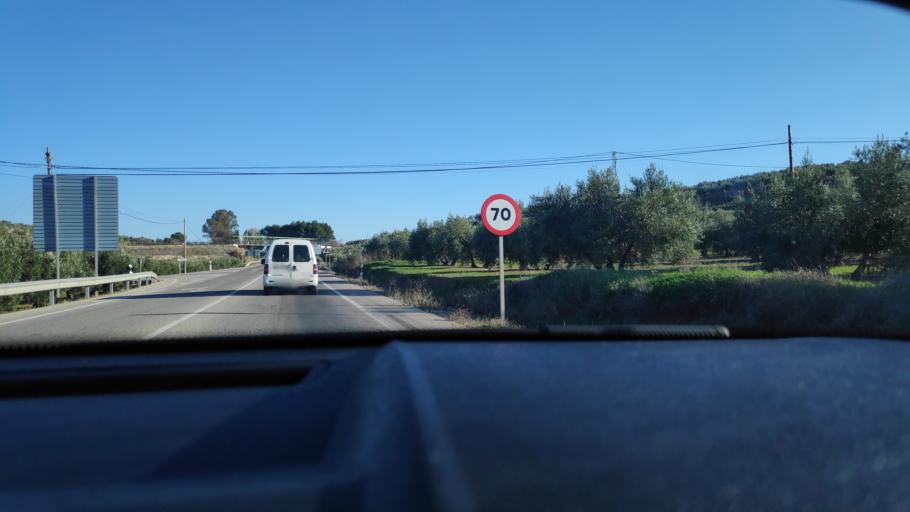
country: ES
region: Andalusia
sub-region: Province of Cordoba
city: Luque
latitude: 37.5751
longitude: -4.2686
